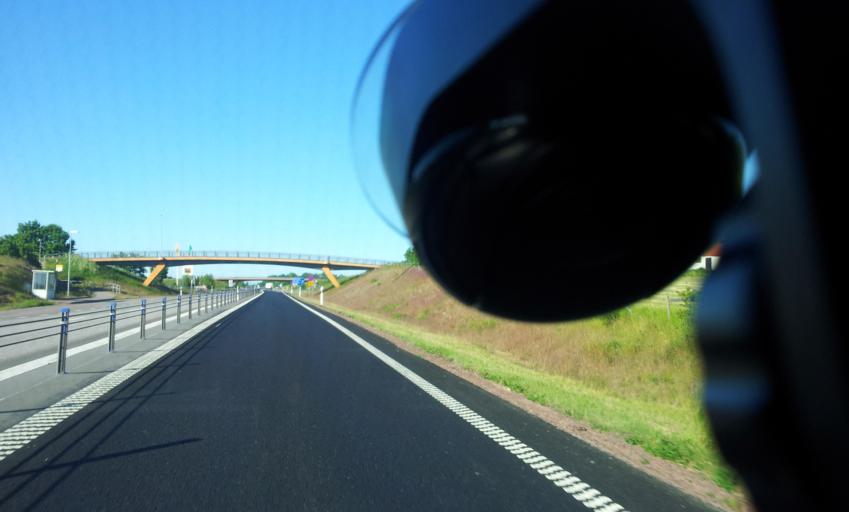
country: SE
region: Kalmar
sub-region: Kalmar Kommun
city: Lindsdal
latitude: 56.7981
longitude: 16.3570
